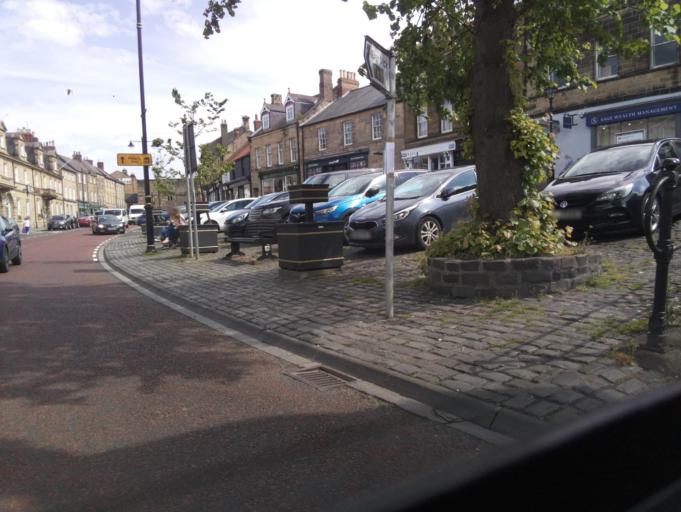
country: GB
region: England
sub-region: Northumberland
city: Alnwick
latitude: 55.4132
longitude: -1.7057
